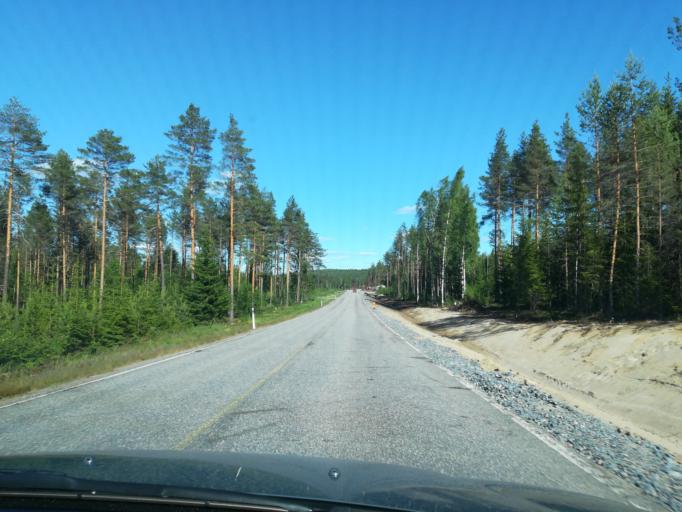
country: FI
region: Southern Savonia
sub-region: Mikkeli
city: Puumala
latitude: 61.4649
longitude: 28.3758
